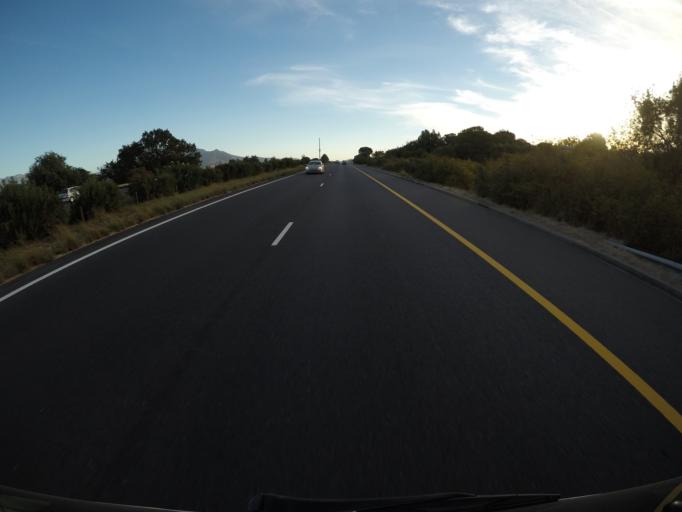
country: ZA
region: Western Cape
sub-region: Cape Winelands District Municipality
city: Paarl
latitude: -33.7760
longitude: 18.9570
